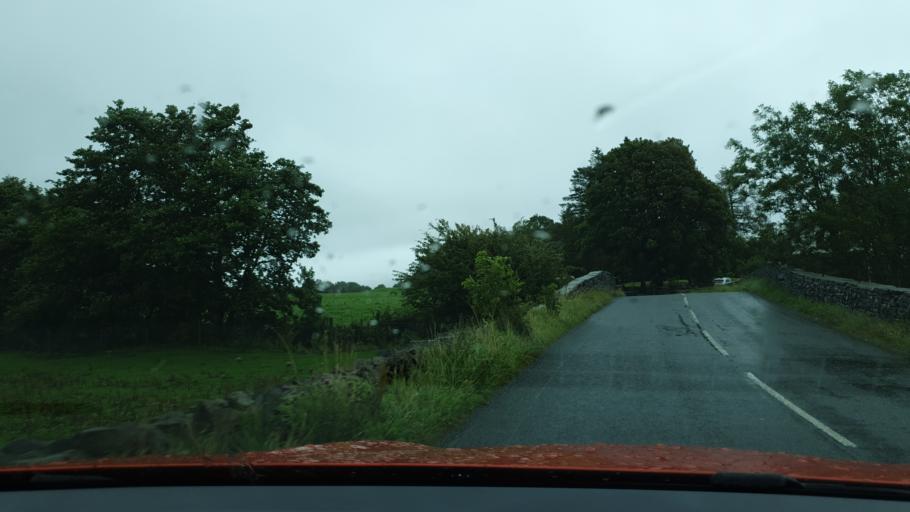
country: GB
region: England
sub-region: Cumbria
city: Ulverston
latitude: 54.3409
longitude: -3.1010
